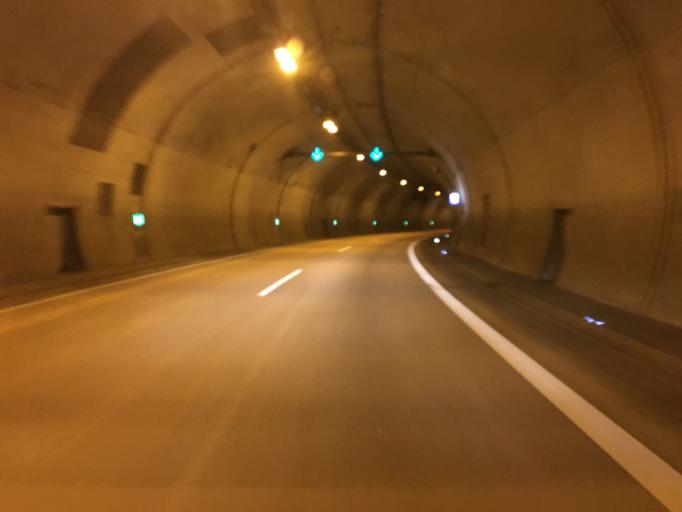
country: DE
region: North Rhine-Westphalia
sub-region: Regierungsbezirk Dusseldorf
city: Wuppertal
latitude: 51.2329
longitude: 7.1211
